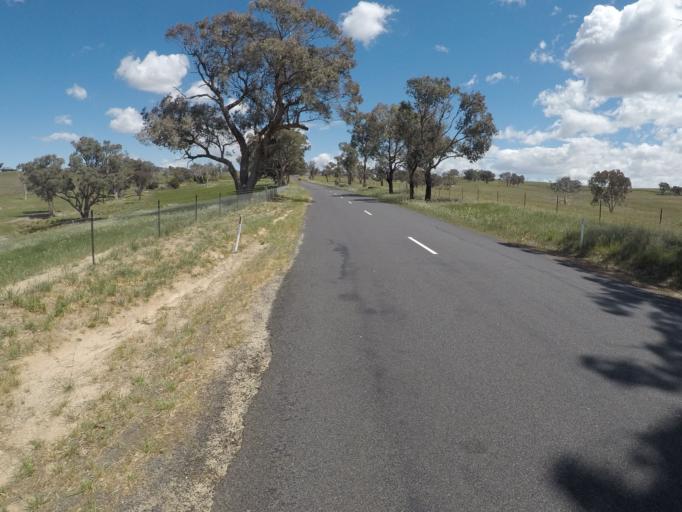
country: AU
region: New South Wales
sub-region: Bathurst Regional
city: Perthville
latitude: -33.5251
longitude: 149.4792
